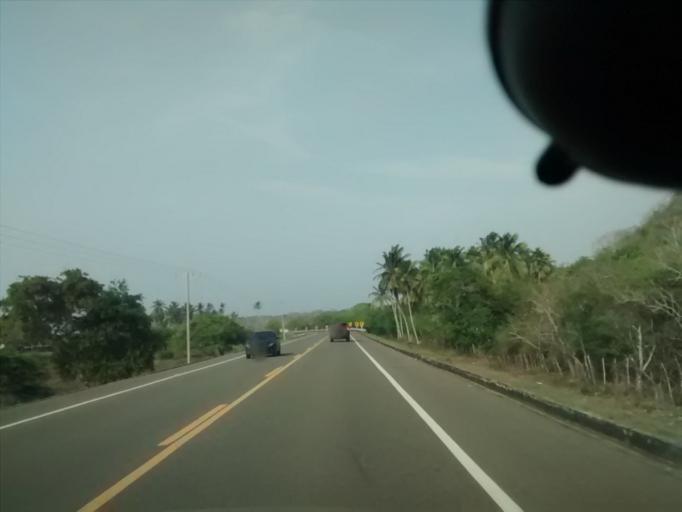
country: CO
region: Bolivar
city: Clemencia
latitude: 10.6290
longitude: -75.4276
